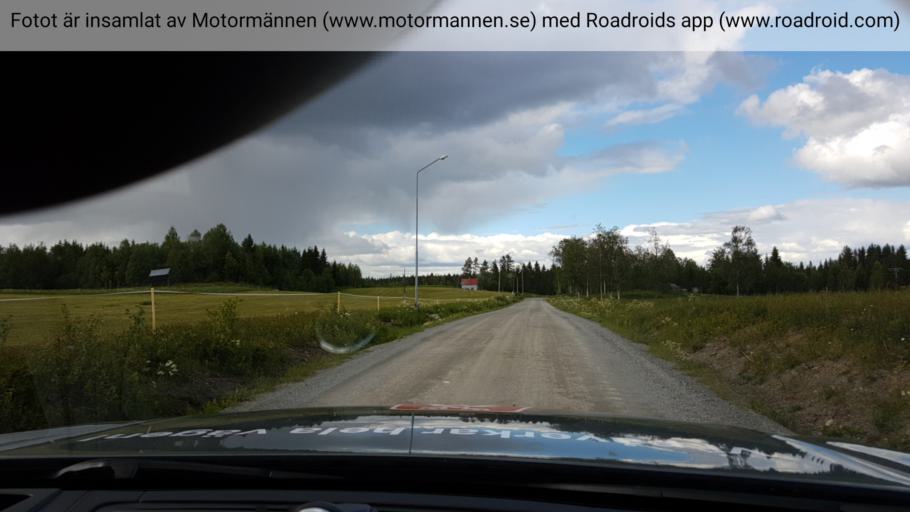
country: SE
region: Jaemtland
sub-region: Bergs Kommun
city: Hoverberg
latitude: 62.9532
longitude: 14.2654
